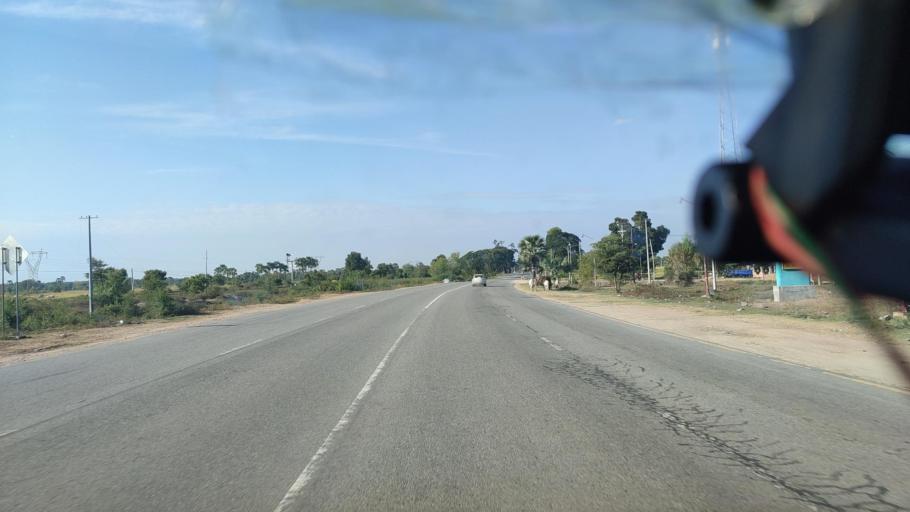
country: MM
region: Mandalay
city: Yamethin
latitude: 20.1924
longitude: 96.1842
